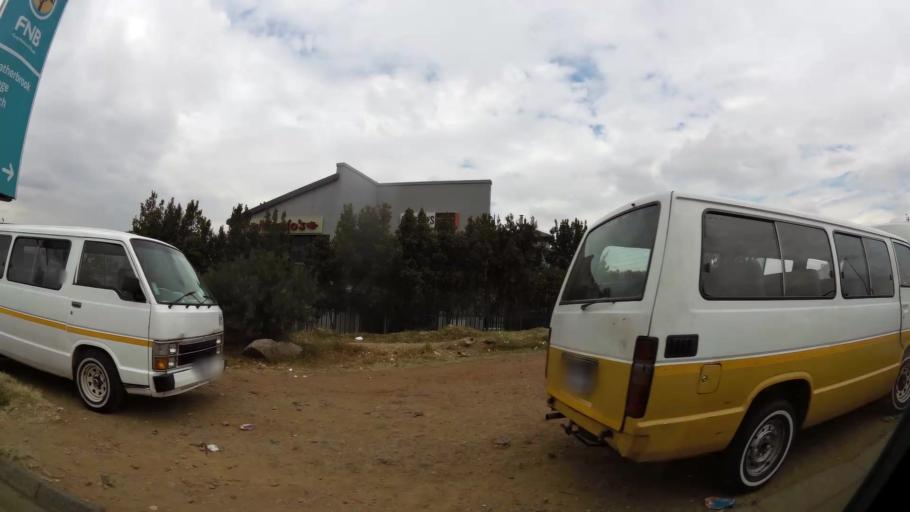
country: ZA
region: Gauteng
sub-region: West Rand District Municipality
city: Muldersdriseloop
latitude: -26.0911
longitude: 27.8700
